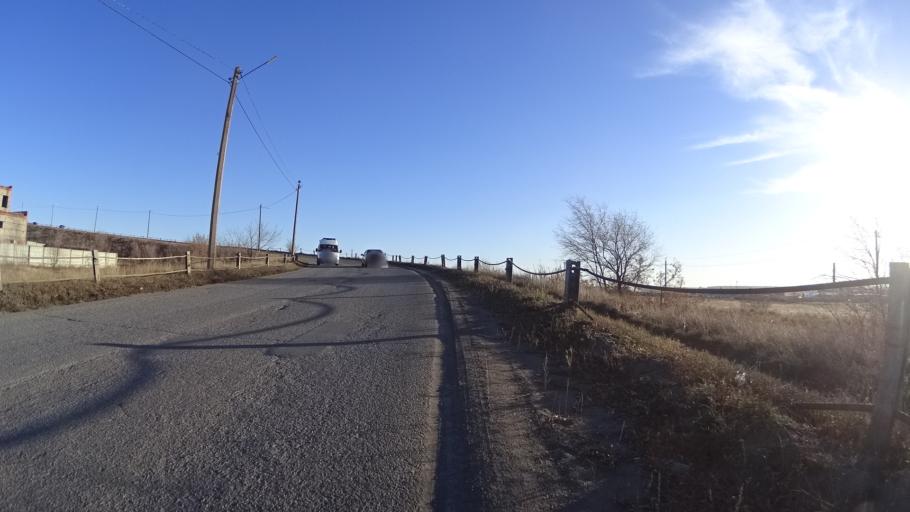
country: RU
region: Chelyabinsk
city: Troitsk
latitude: 54.0803
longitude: 61.5980
